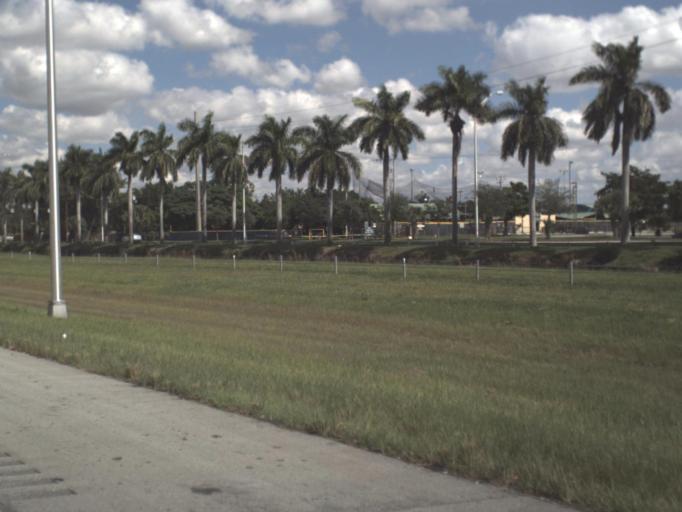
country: US
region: Florida
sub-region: Miami-Dade County
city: University Park
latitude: 25.7466
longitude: -80.3846
